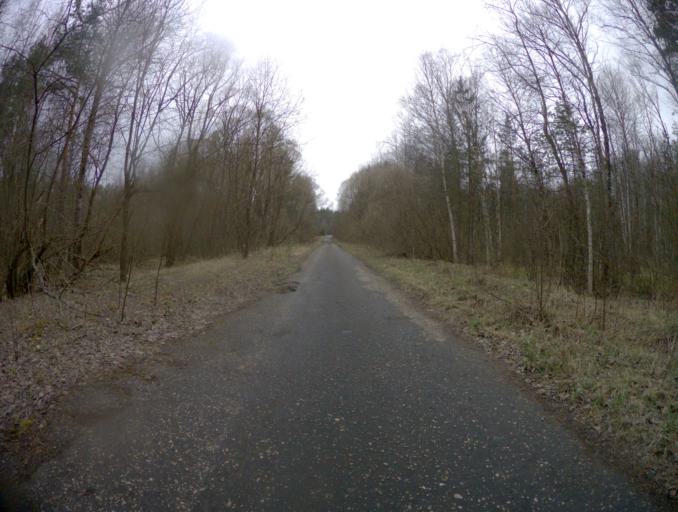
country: RU
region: Vladimir
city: Sudogda
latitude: 55.9720
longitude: 40.7982
